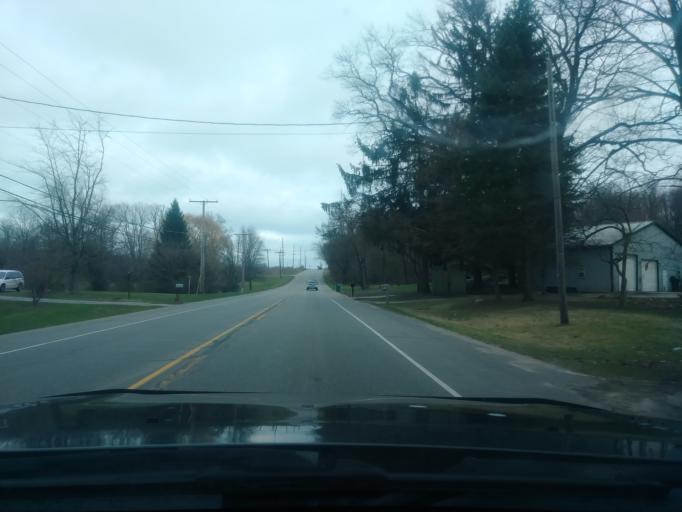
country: US
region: Indiana
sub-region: LaPorte County
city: Trail Creek
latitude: 41.6462
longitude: -86.8041
